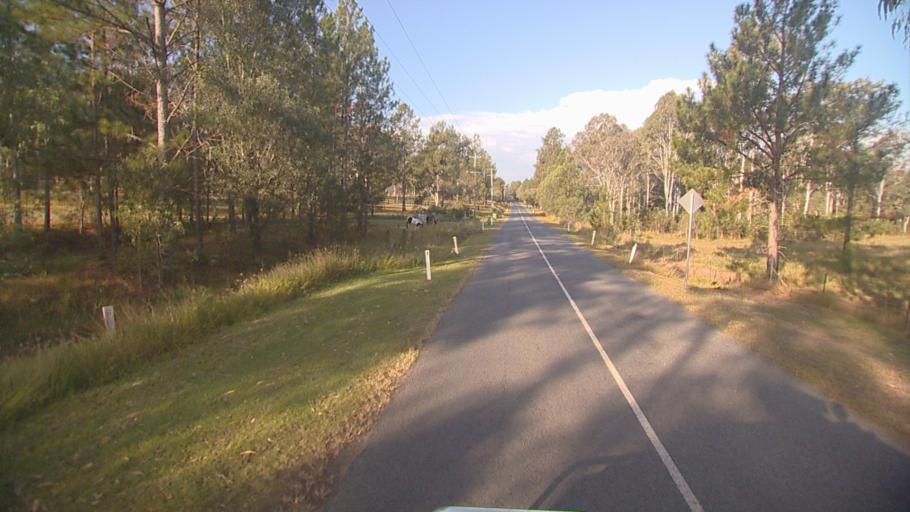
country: AU
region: Queensland
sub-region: Logan
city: Cedar Vale
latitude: -27.8494
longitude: 153.1155
